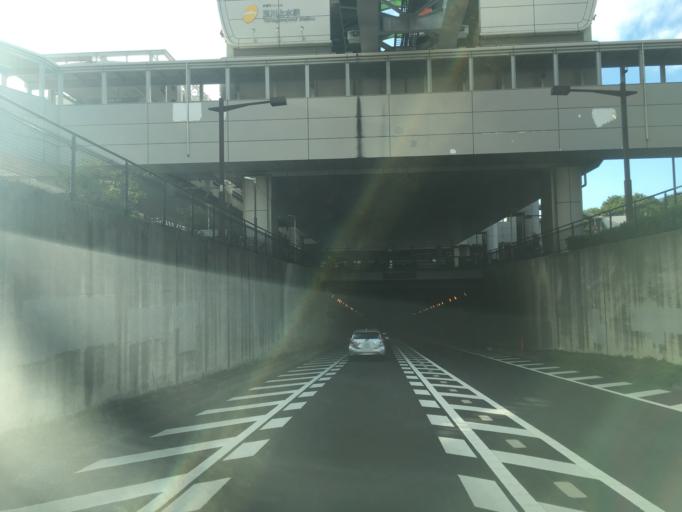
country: JP
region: Tokyo
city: Higashimurayama-shi
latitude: 35.7328
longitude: 139.4178
